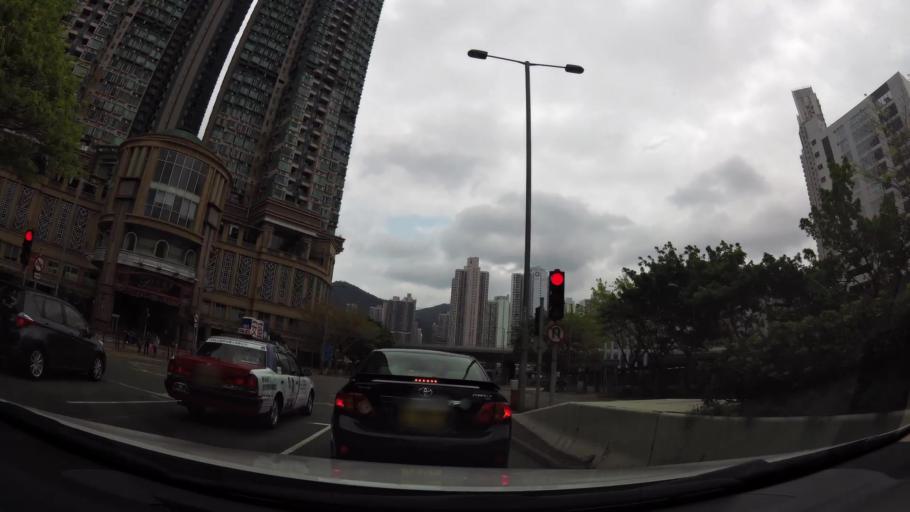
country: HK
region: Sham Shui Po
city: Sham Shui Po
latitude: 22.3333
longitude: 114.1498
